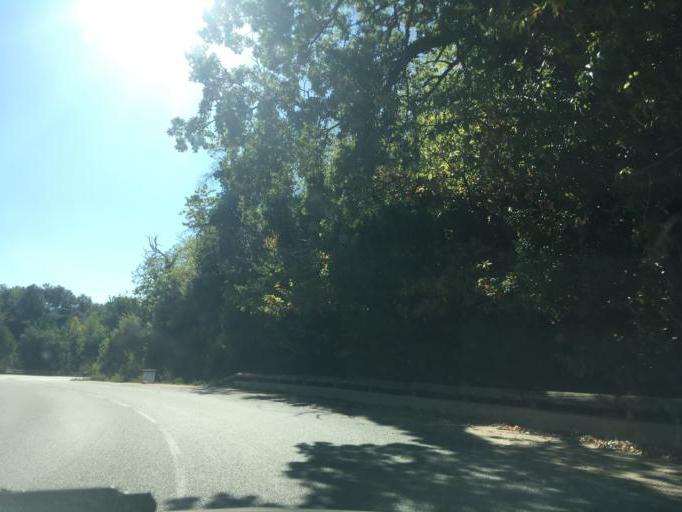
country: FR
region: Provence-Alpes-Cote d'Azur
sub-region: Departement du Var
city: La Garde-Freinet
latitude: 43.3005
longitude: 6.4749
